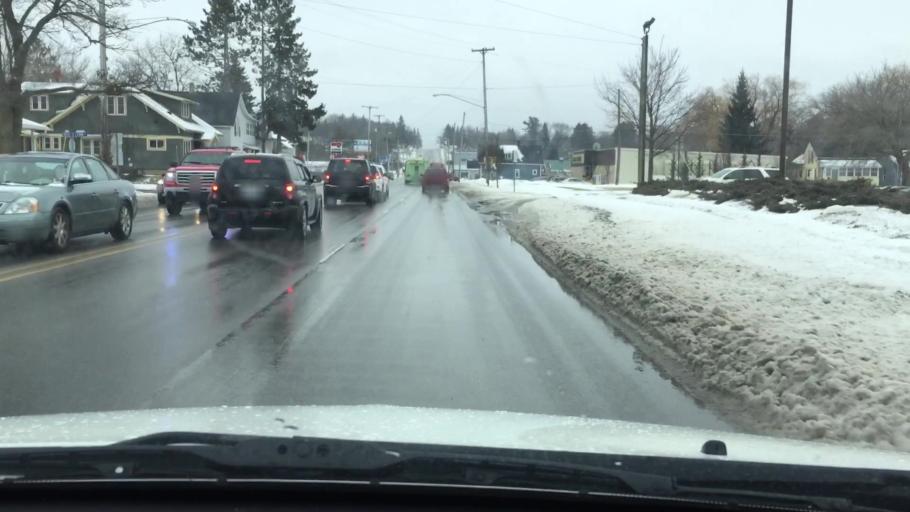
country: US
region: Michigan
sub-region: Wexford County
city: Cadillac
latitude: 44.2449
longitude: -85.3965
